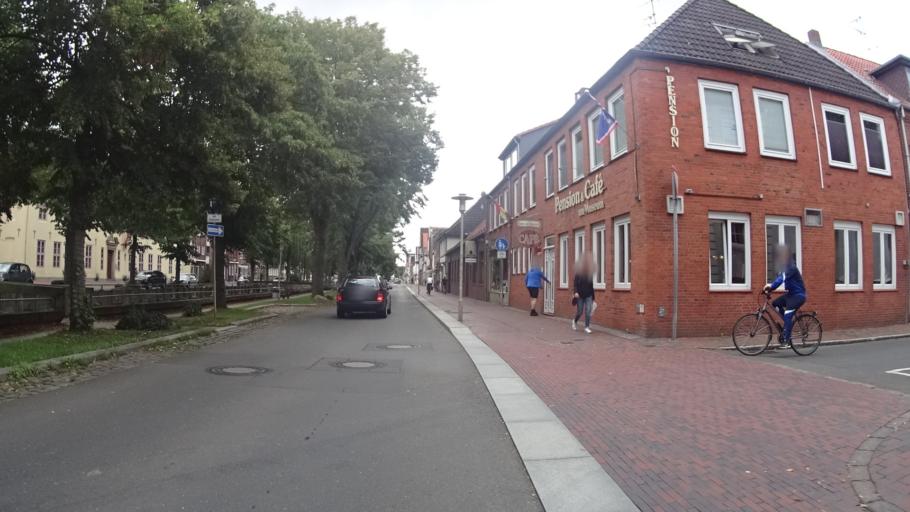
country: DE
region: Schleswig-Holstein
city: Gluckstadt
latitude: 53.7890
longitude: 9.4210
